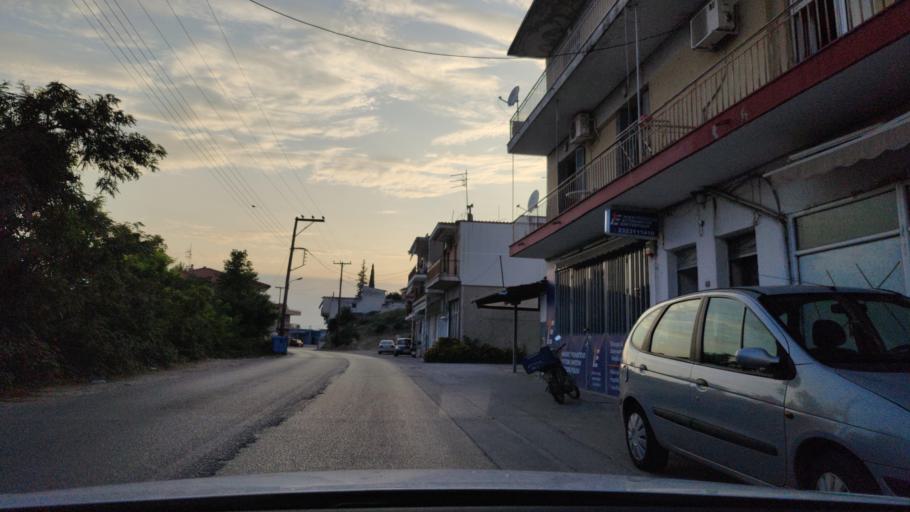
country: GR
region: Central Macedonia
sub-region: Nomos Serron
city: Sidirokastro
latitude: 41.2402
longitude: 23.3908
